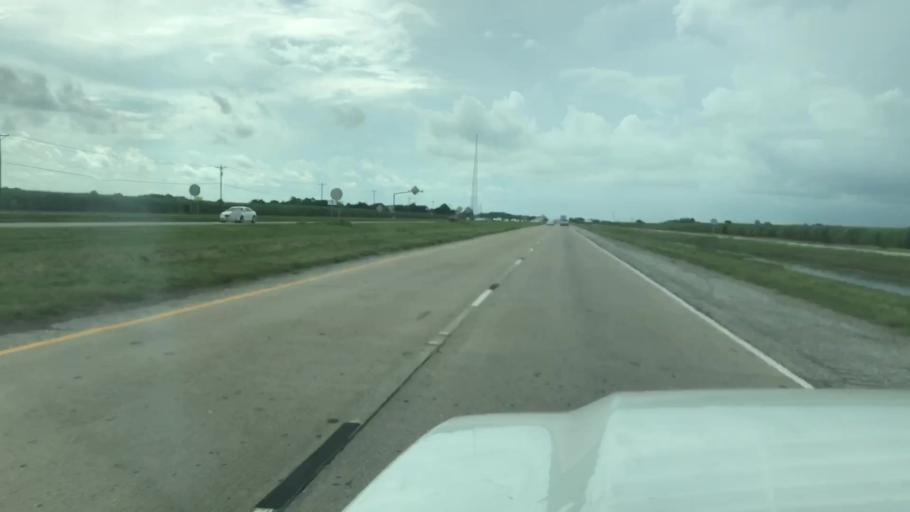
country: US
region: Louisiana
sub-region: Iberia Parish
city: Jeanerette
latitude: 29.9127
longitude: -91.7178
